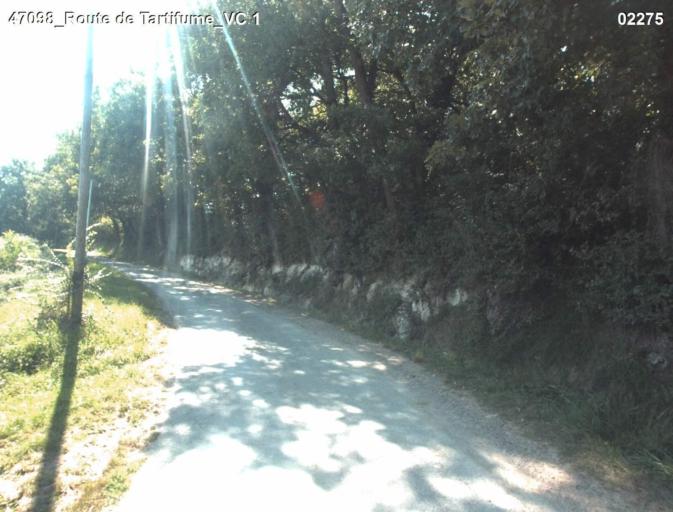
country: FR
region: Aquitaine
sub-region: Departement du Lot-et-Garonne
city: Nerac
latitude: 44.0928
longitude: 0.4043
